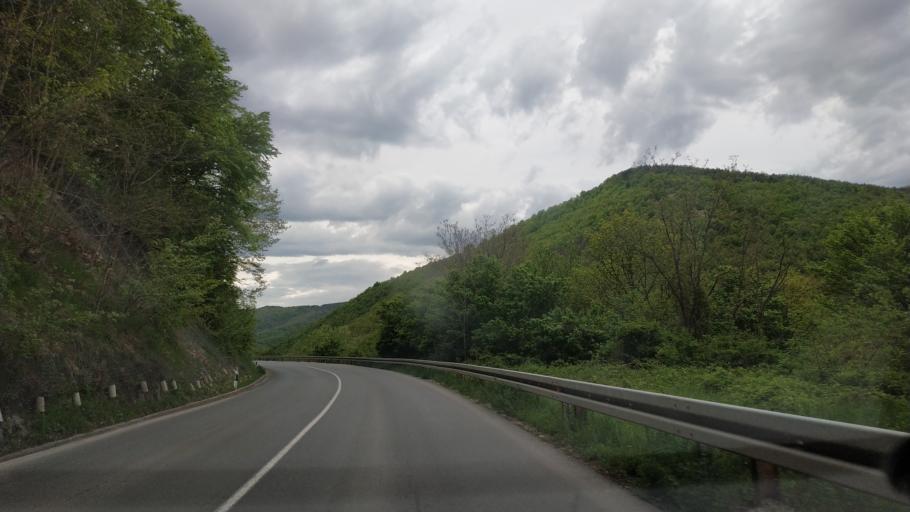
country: RS
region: Central Serbia
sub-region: Nisavski Okrug
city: Aleksinac
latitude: 43.6502
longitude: 21.7398
